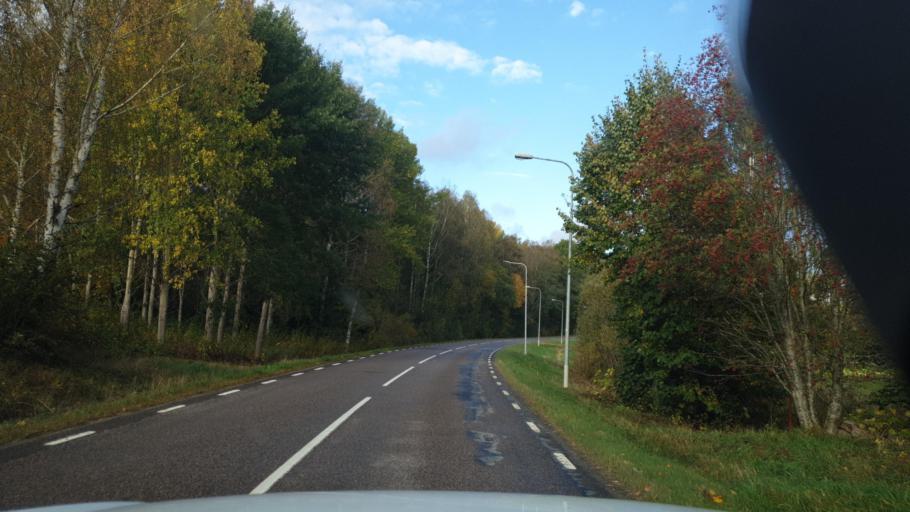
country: SE
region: Vaermland
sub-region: Arvika Kommun
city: Arvika
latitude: 59.4871
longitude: 12.6894
